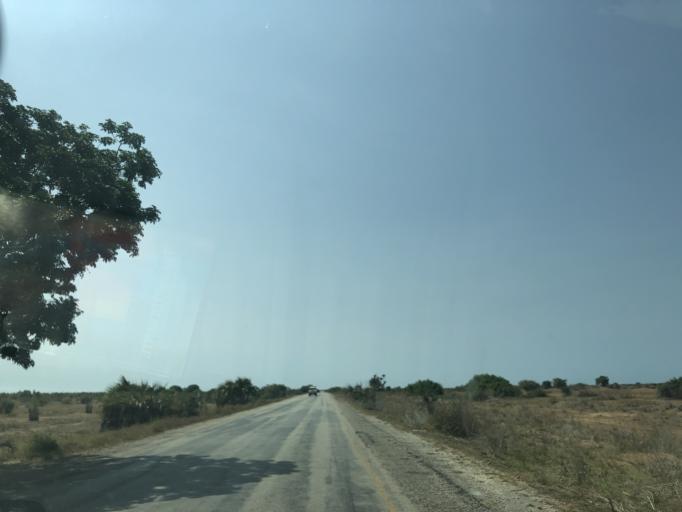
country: AO
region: Cuanza Sul
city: Sumbe
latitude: -10.5280
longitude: 13.7269
